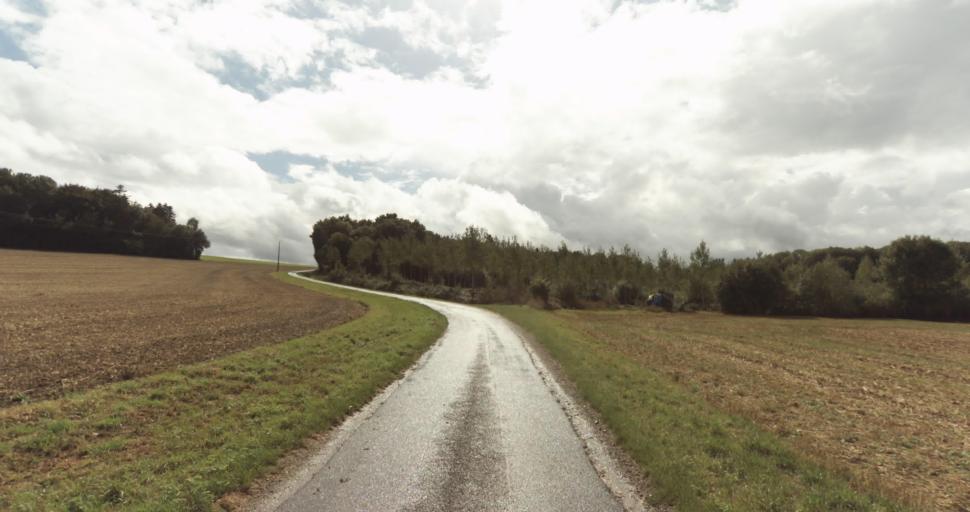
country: FR
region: Lower Normandy
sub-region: Departement de l'Orne
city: Sainte-Gauburge-Sainte-Colombe
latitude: 48.7010
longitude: 0.4072
